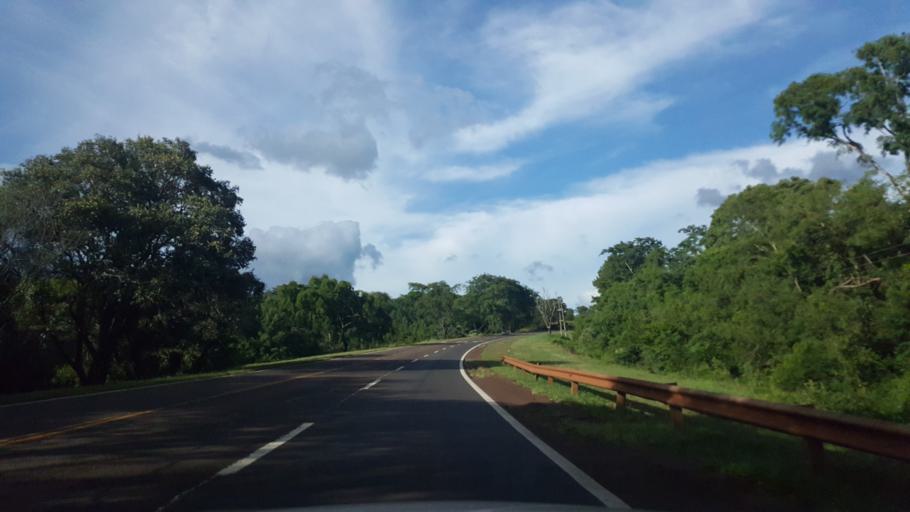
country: AR
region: Misiones
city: Santa Ana
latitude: -27.3592
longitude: -55.5571
